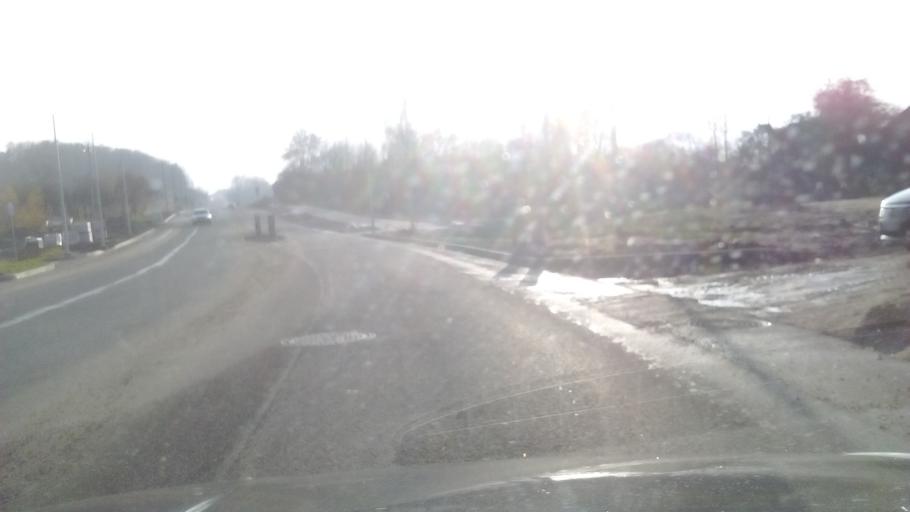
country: LT
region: Alytaus apskritis
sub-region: Alytus
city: Alytus
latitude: 54.4089
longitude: 24.0045
